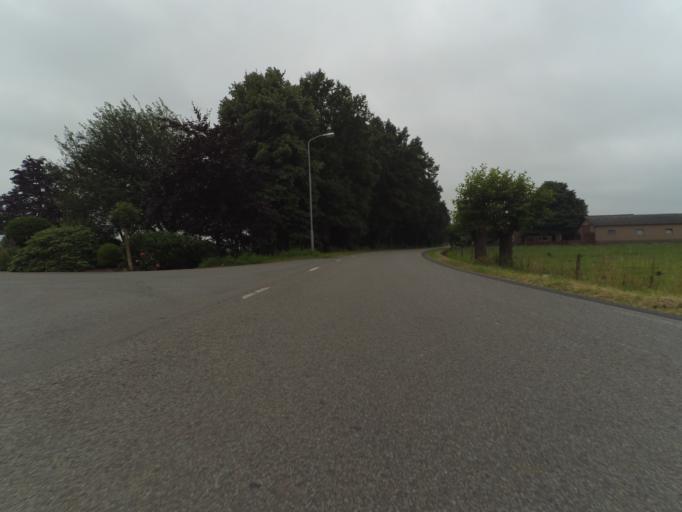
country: NL
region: Gelderland
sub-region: Gemeente Barneveld
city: Kootwijkerbroek
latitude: 52.1549
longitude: 5.6487
